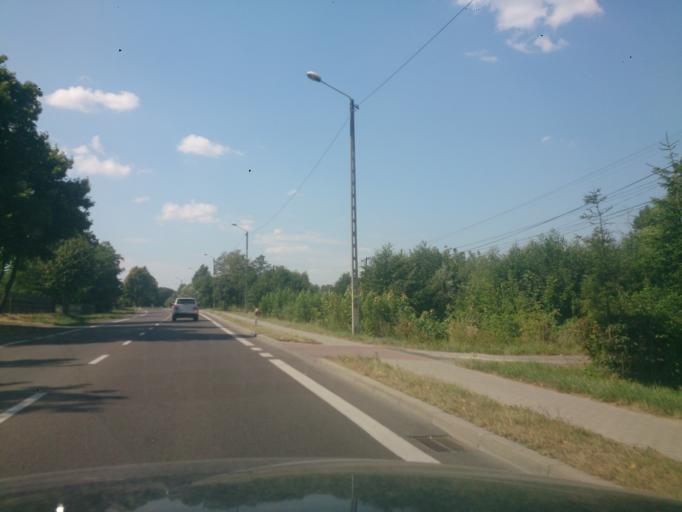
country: PL
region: Subcarpathian Voivodeship
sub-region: Powiat kolbuszowski
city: Dzikowiec
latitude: 50.2006
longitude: 21.8690
